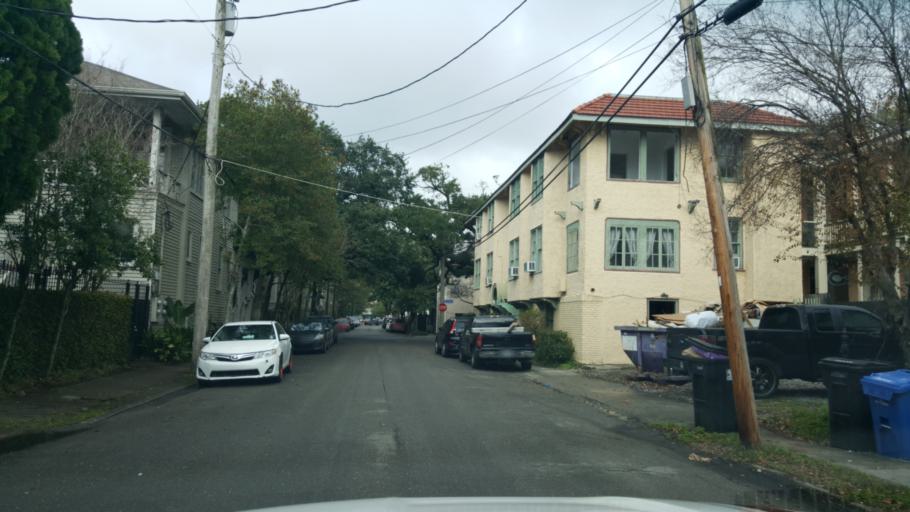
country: US
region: Louisiana
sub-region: Orleans Parish
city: New Orleans
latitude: 29.9359
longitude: -90.0752
